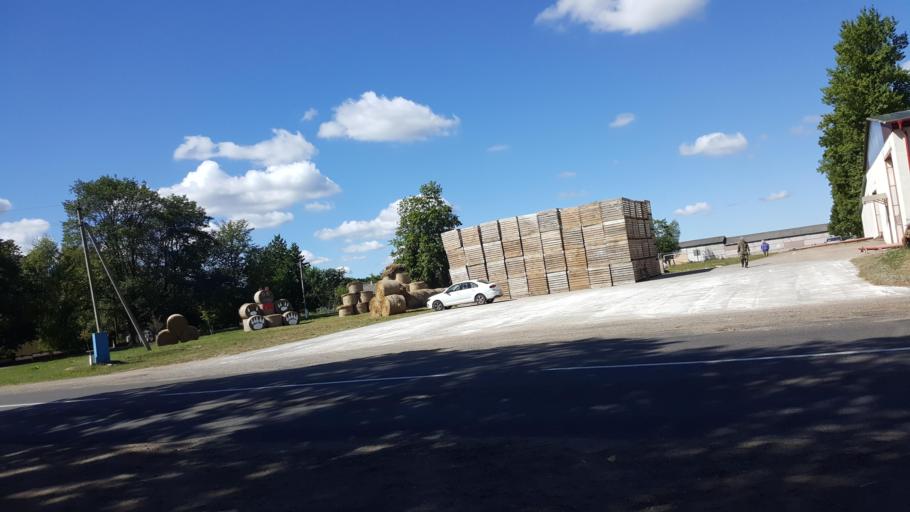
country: BY
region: Brest
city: Vysokaye
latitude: 52.3476
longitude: 23.3458
